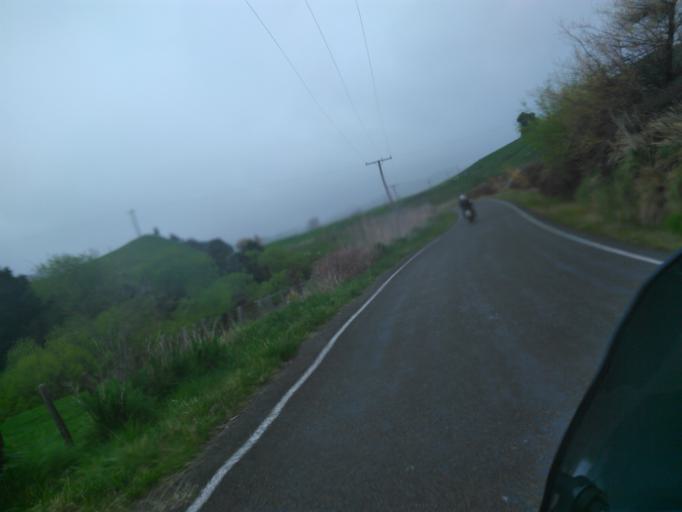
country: NZ
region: Gisborne
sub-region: Gisborne District
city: Gisborne
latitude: -38.6482
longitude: 177.7188
